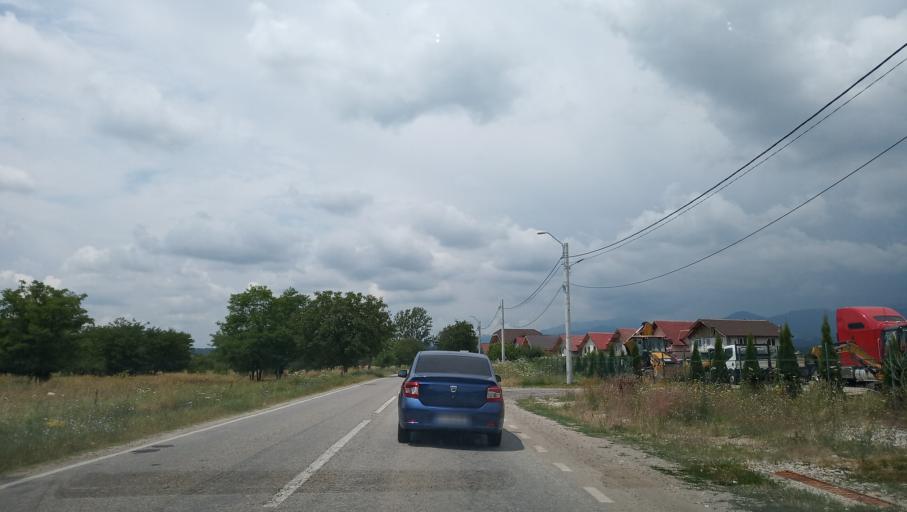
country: RO
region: Gorj
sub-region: Comuna Arcani
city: Arcani
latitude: 45.0871
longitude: 23.1586
